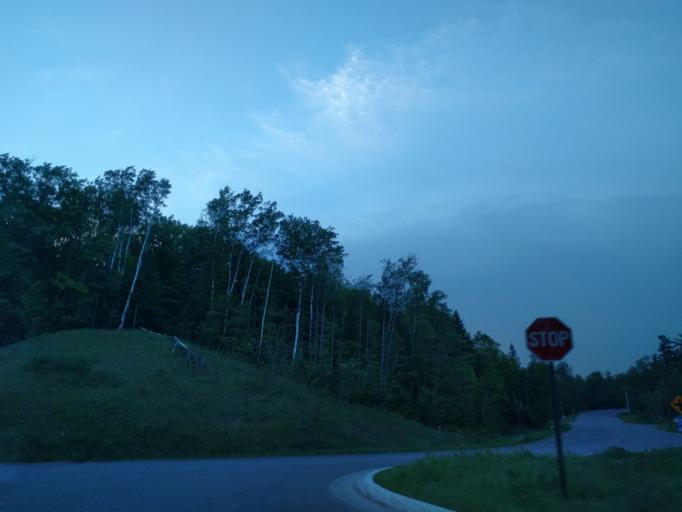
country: US
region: Michigan
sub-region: Marquette County
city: Trowbridge Park
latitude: 46.5565
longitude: -87.4582
